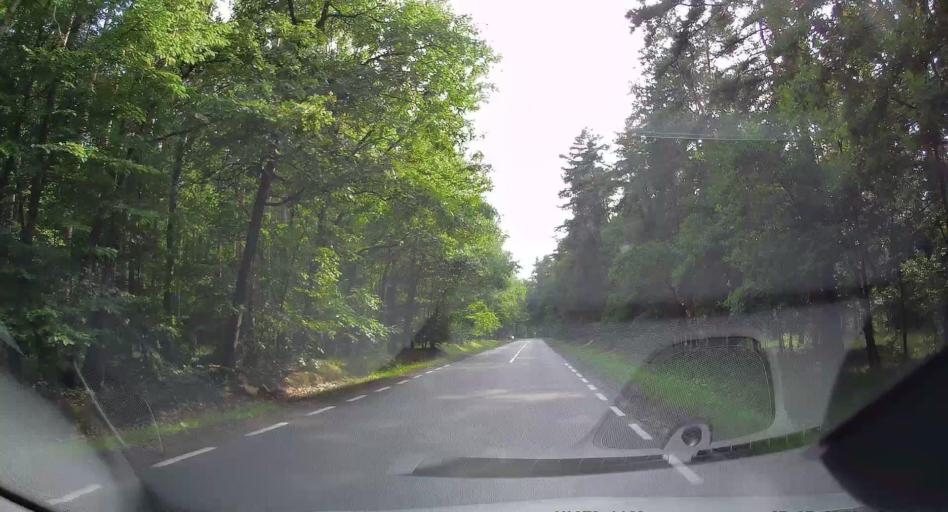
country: PL
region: Lodz Voivodeship
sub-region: Powiat tomaszowski
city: Rzeczyca
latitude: 51.5740
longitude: 20.2793
